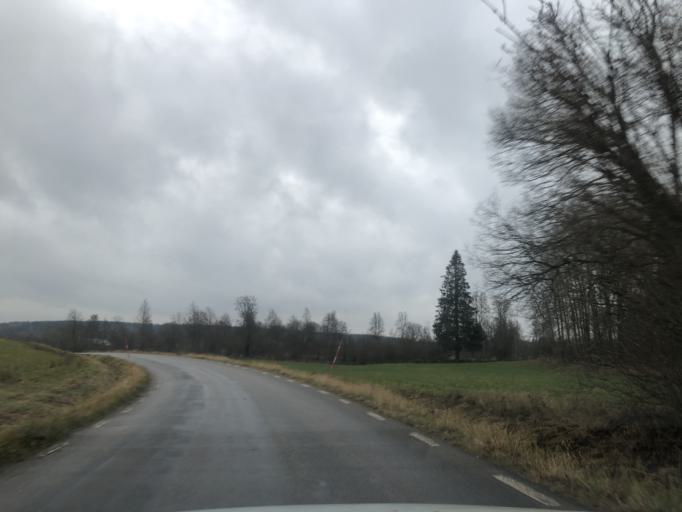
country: SE
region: Vaestra Goetaland
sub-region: Ulricehamns Kommun
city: Ulricehamn
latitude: 57.8906
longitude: 13.5101
